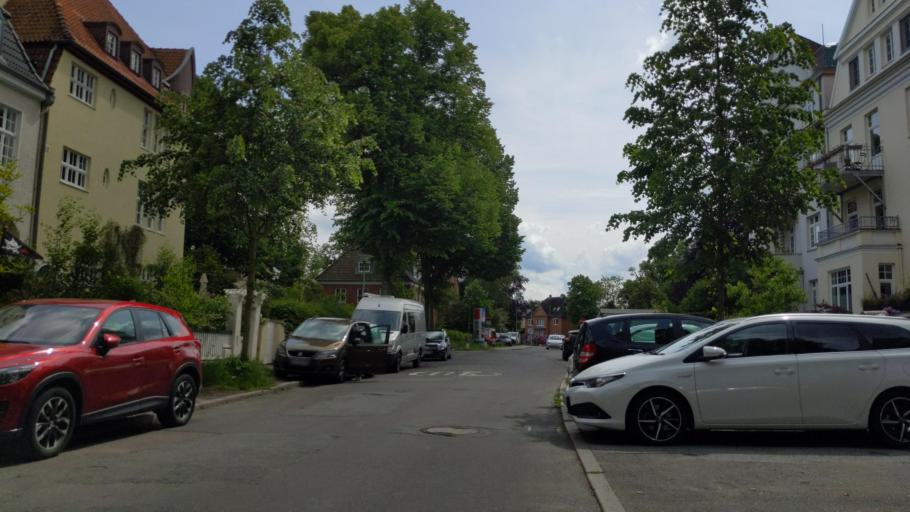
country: DE
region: Schleswig-Holstein
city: Luebeck
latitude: 53.8564
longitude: 10.6979
